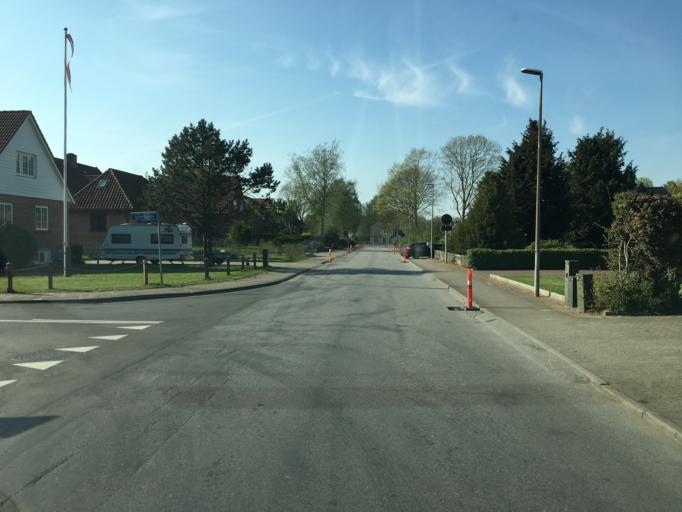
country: DK
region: South Denmark
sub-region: Haderslev Kommune
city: Vojens
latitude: 55.2473
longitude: 9.3138
